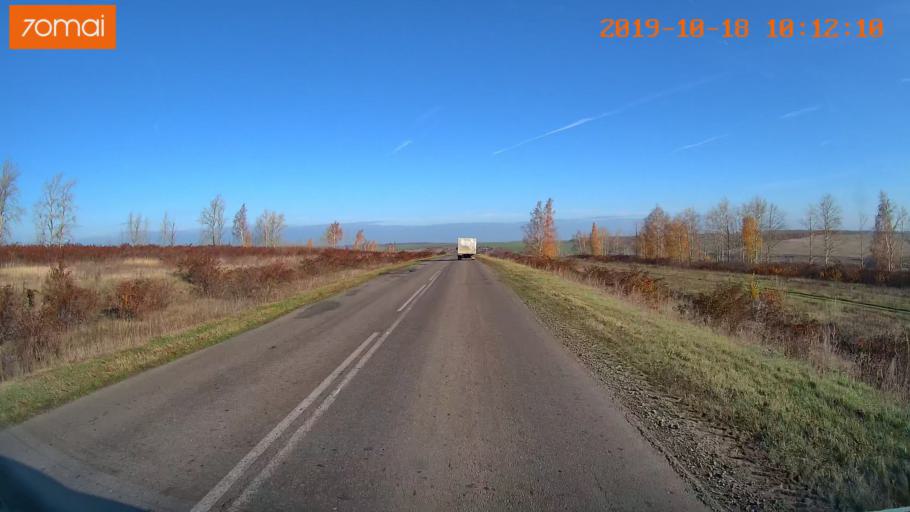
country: RU
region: Tula
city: Kurkino
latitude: 53.3909
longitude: 38.5056
